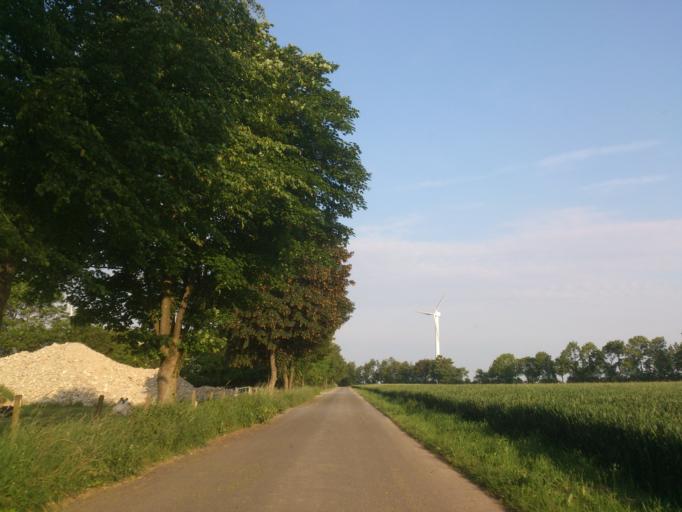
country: DE
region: North Rhine-Westphalia
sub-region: Regierungsbezirk Detmold
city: Altenbeken
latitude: 51.7211
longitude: 8.8821
